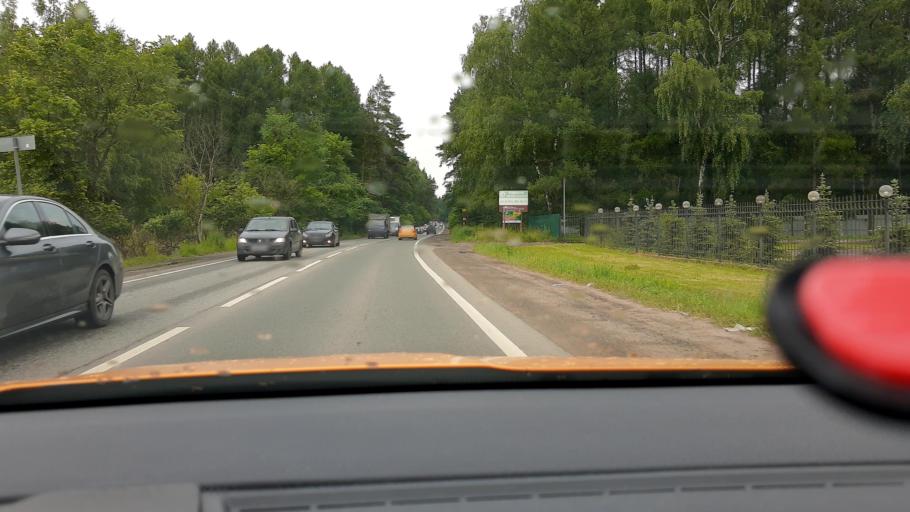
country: RU
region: Moskovskaya
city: Pirogovskiy
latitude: 55.9897
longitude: 37.7269
